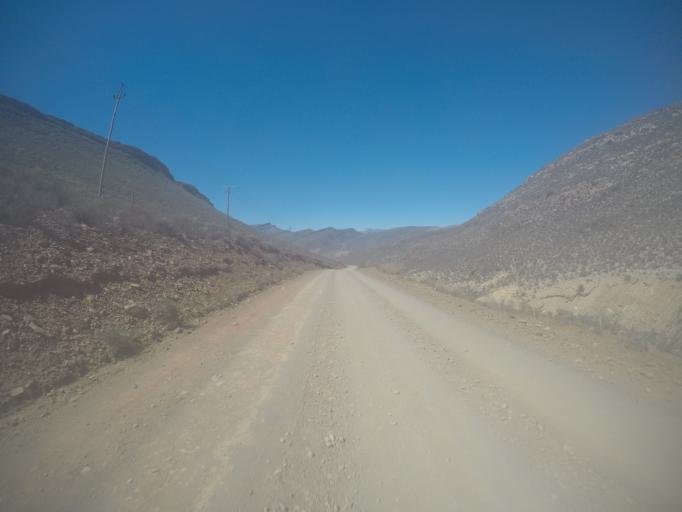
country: ZA
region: Western Cape
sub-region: West Coast District Municipality
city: Clanwilliam
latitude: -32.5367
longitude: 19.3557
